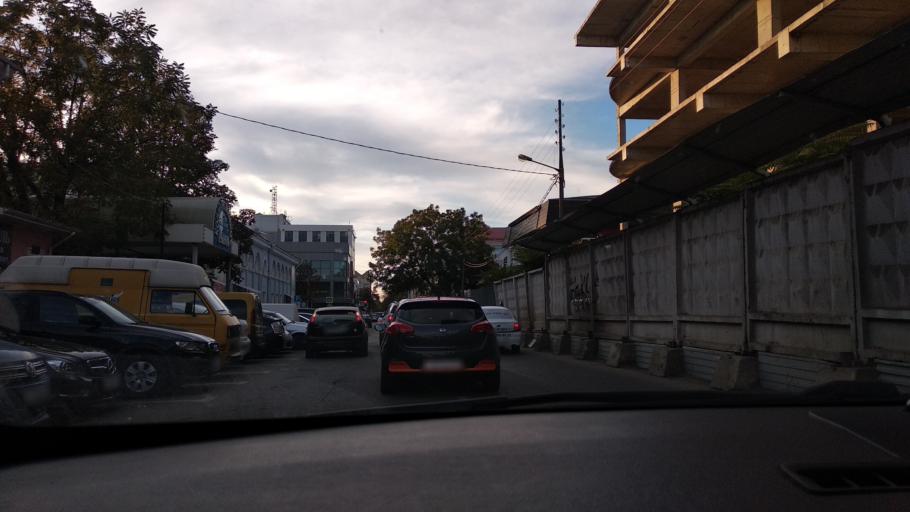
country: RU
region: Krasnodarskiy
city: Krasnodar
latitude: 45.0278
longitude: 38.9753
